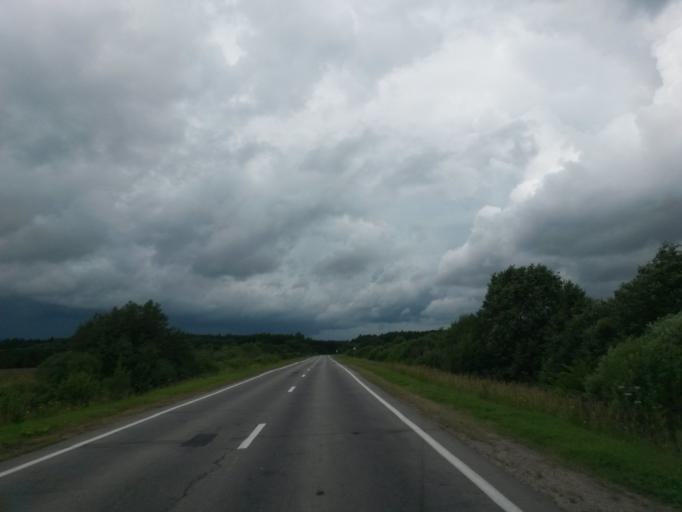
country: RU
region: Jaroslavl
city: Konstantinovskiy
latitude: 57.8497
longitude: 39.6302
